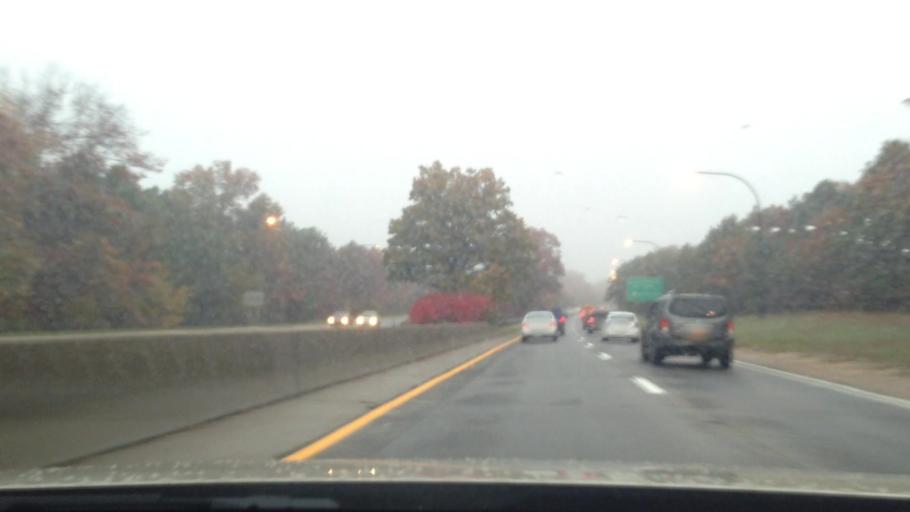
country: US
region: New York
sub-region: Suffolk County
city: Bay Wood
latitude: 40.7753
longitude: -73.2802
